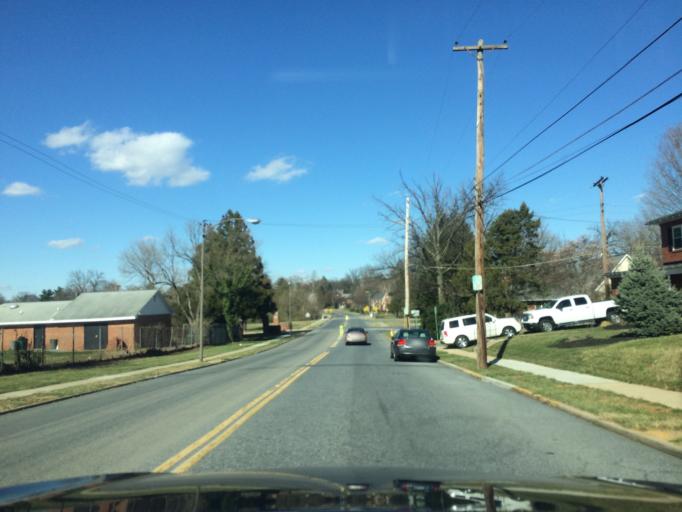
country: US
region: Maryland
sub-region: Frederick County
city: Frederick
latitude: 39.4145
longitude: -77.4248
